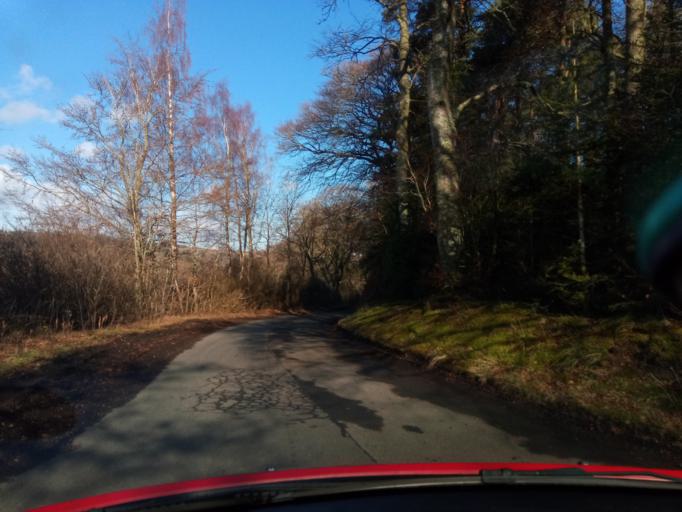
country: GB
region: Scotland
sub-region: The Scottish Borders
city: Hawick
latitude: 55.5057
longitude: -2.7625
